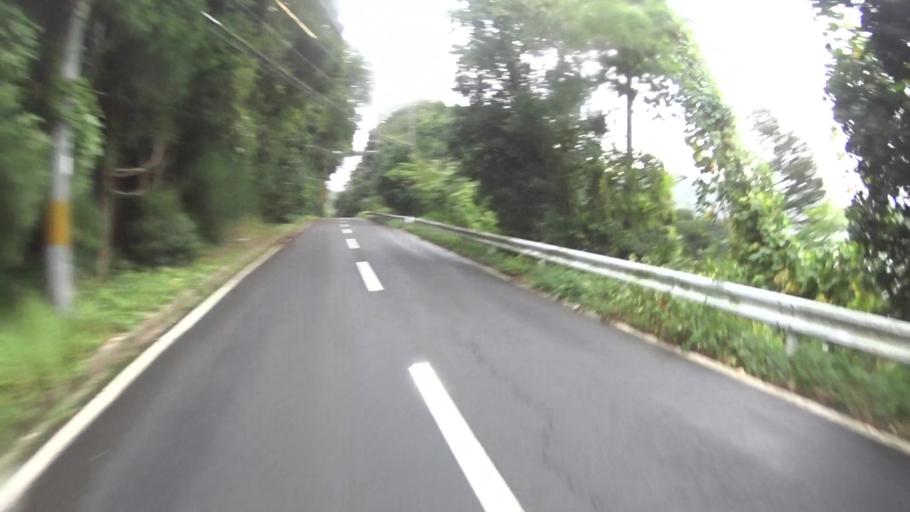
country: JP
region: Kyoto
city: Miyazu
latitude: 35.5580
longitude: 135.2391
